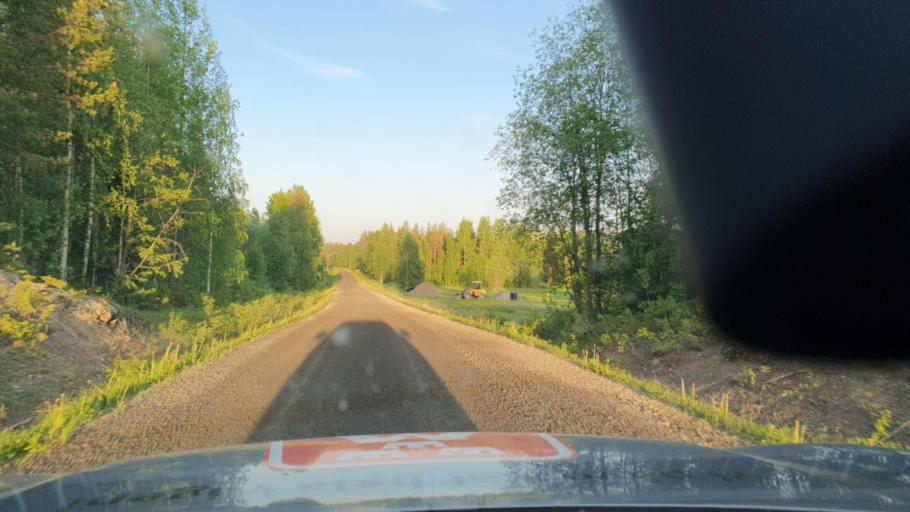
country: SE
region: Norrbotten
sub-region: Bodens Kommun
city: Boden
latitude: 66.0577
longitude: 21.7386
